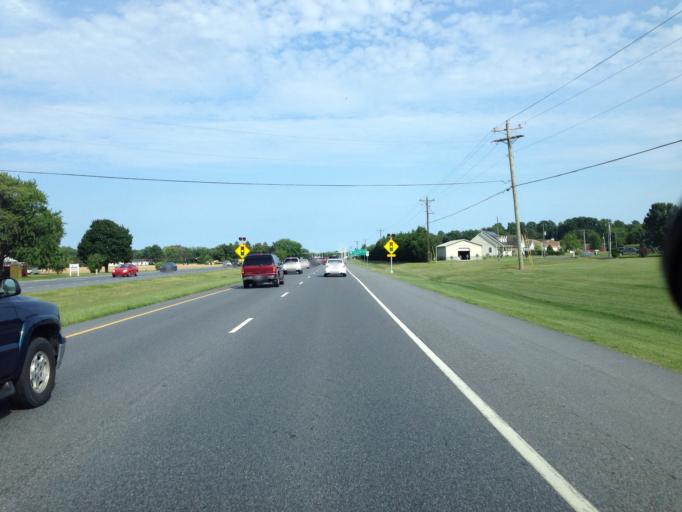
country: US
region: Delaware
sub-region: Sussex County
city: Milton
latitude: 38.8069
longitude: -75.2775
